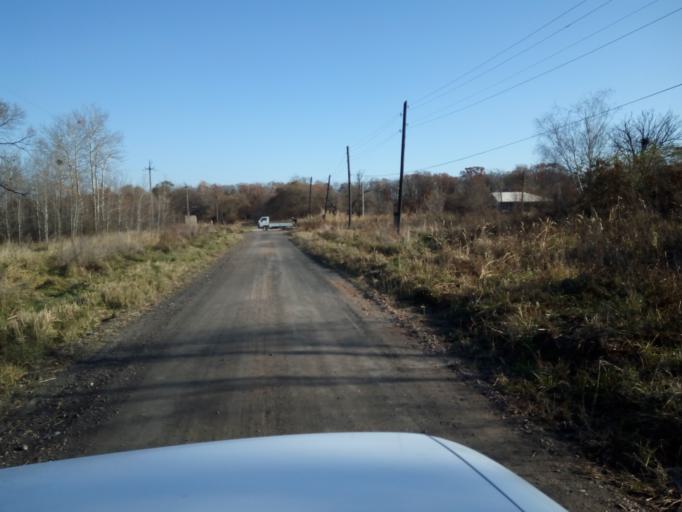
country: RU
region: Primorskiy
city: Lazo
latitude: 45.8766
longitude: 133.6555
